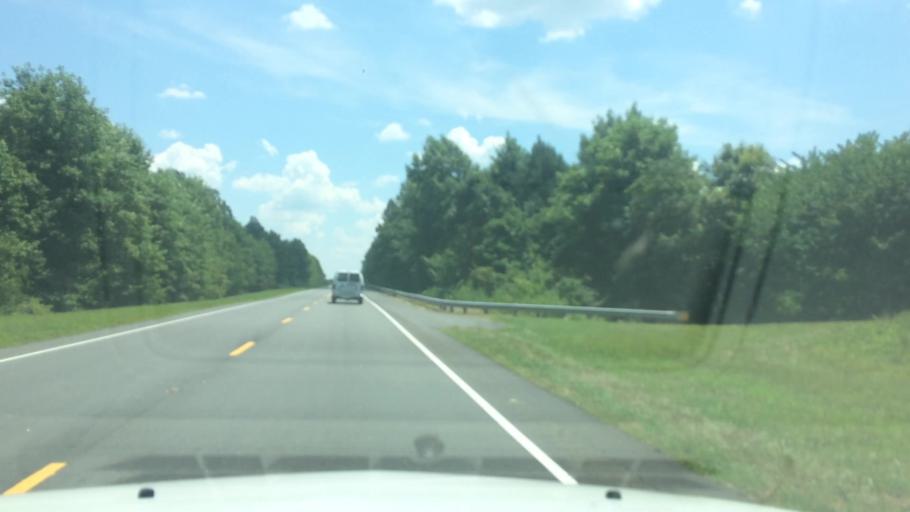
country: US
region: North Carolina
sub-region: Alexander County
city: Stony Point
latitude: 35.8412
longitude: -81.0256
